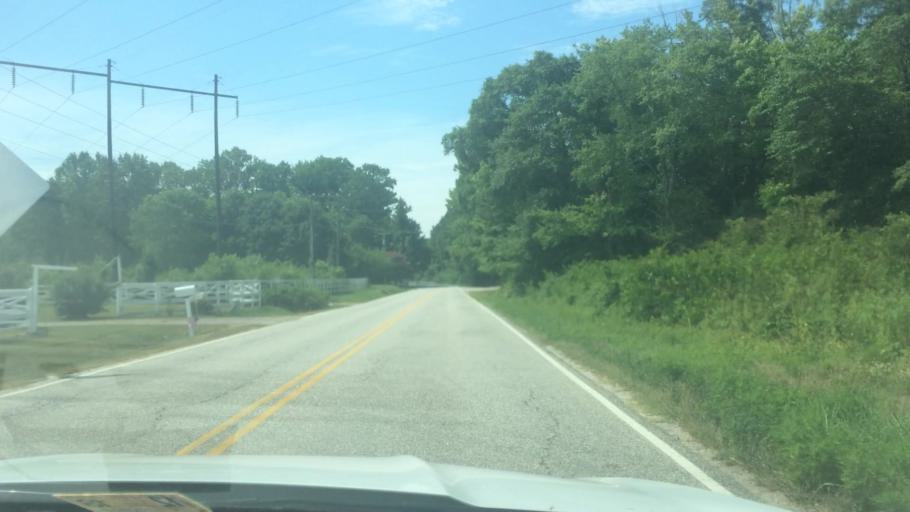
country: US
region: Virginia
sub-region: City of Poquoson
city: Poquoson
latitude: 37.1197
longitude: -76.4321
